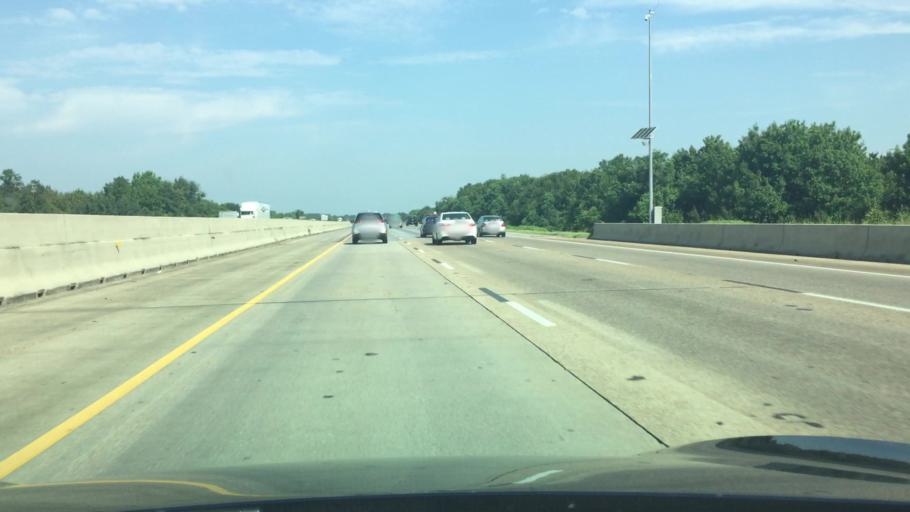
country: US
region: Alabama
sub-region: Montgomery County
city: Montgomery
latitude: 32.3992
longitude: -86.3347
